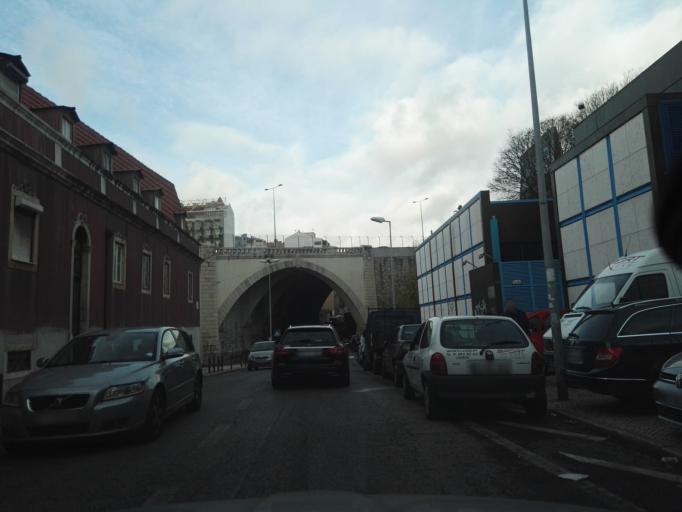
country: PT
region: Lisbon
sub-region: Lisbon
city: Lisbon
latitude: 38.7224
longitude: -9.1668
